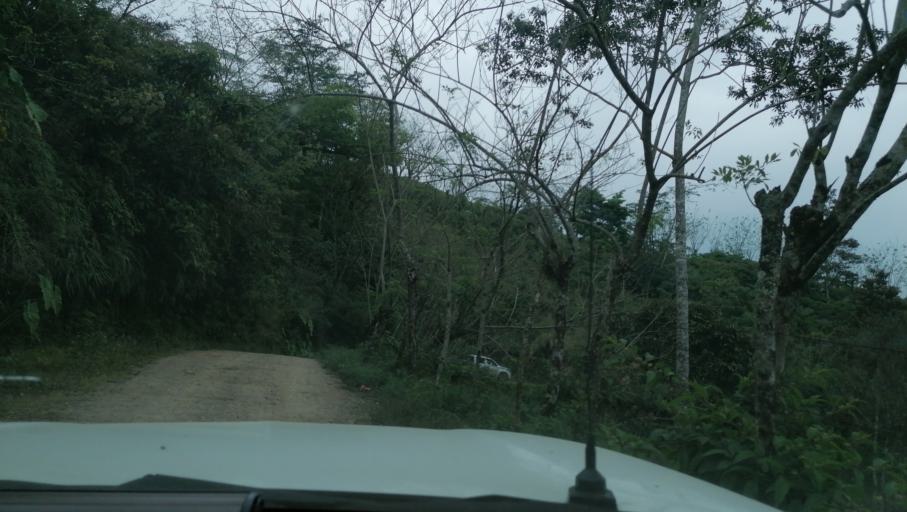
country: MX
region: Chiapas
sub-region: Francisco Leon
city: San Miguel la Sardina
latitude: 17.3344
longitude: -93.3130
